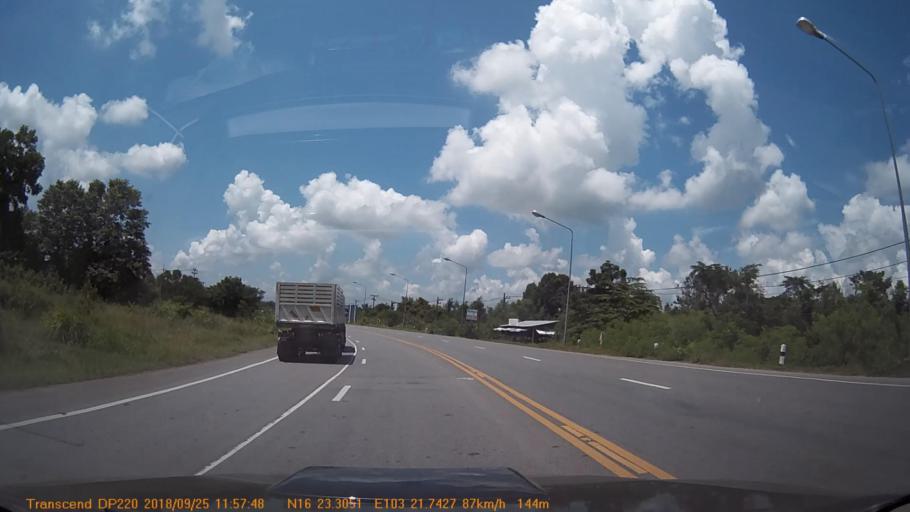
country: TH
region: Kalasin
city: Yang Talat
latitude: 16.3883
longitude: 103.3621
